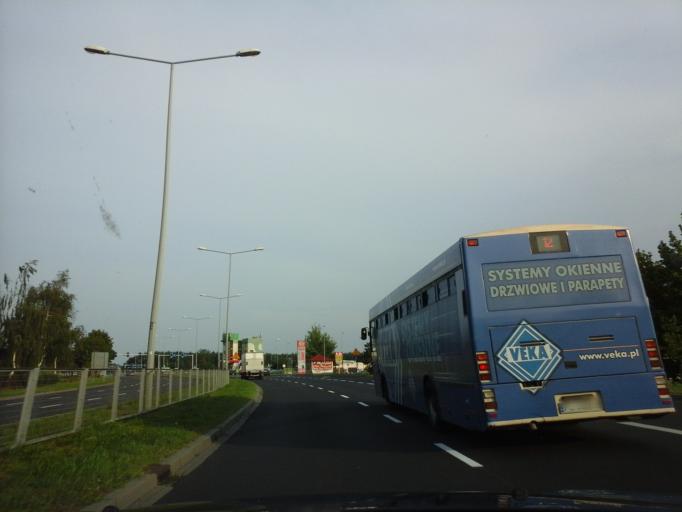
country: PL
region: Greater Poland Voivodeship
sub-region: Leszno
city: Leszno
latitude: 51.8291
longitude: 16.5986
